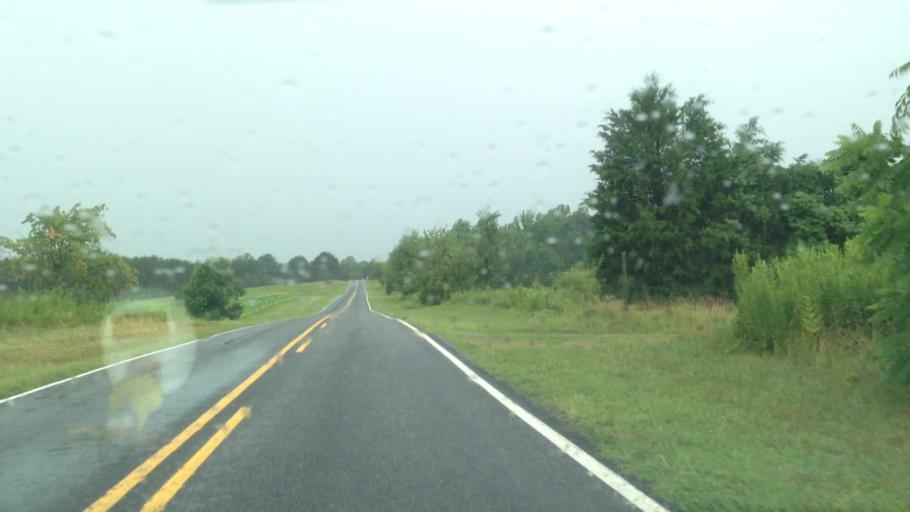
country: US
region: North Carolina
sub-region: Stokes County
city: Danbury
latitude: 36.4446
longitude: -80.0933
